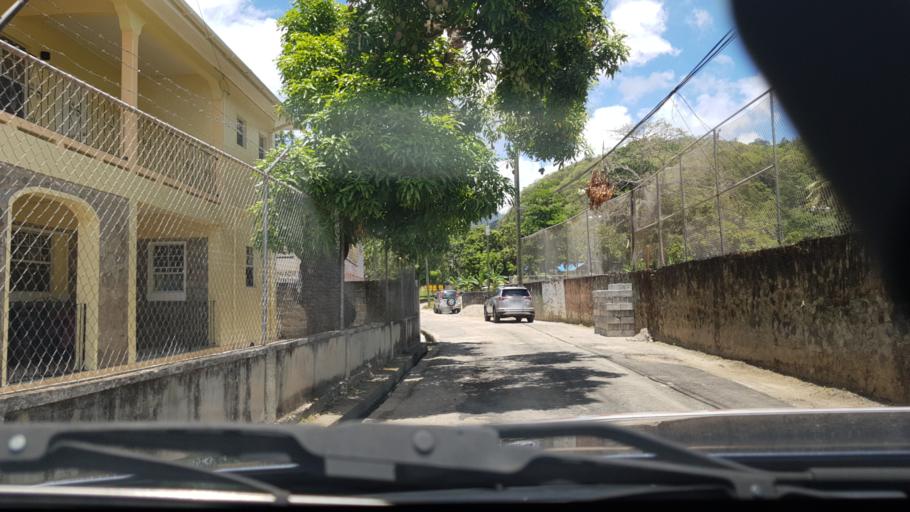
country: LC
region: Anse-la-Raye
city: Canaries
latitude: 13.9039
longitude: -61.0664
